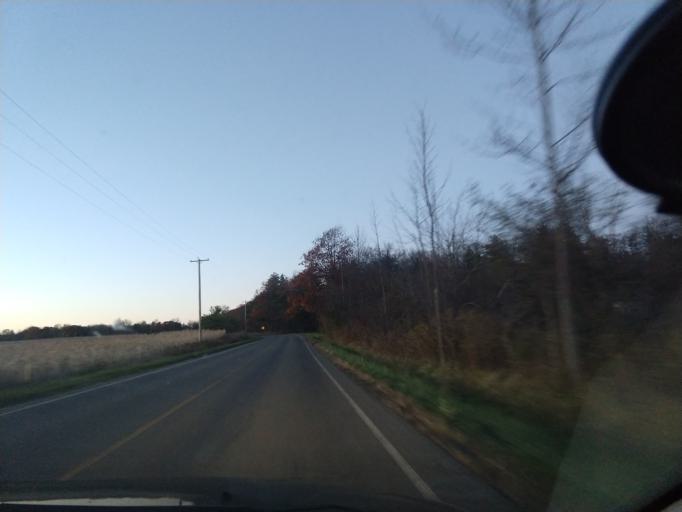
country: US
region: New York
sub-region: Tompkins County
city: Northeast Ithaca
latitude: 42.4639
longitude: -76.4454
